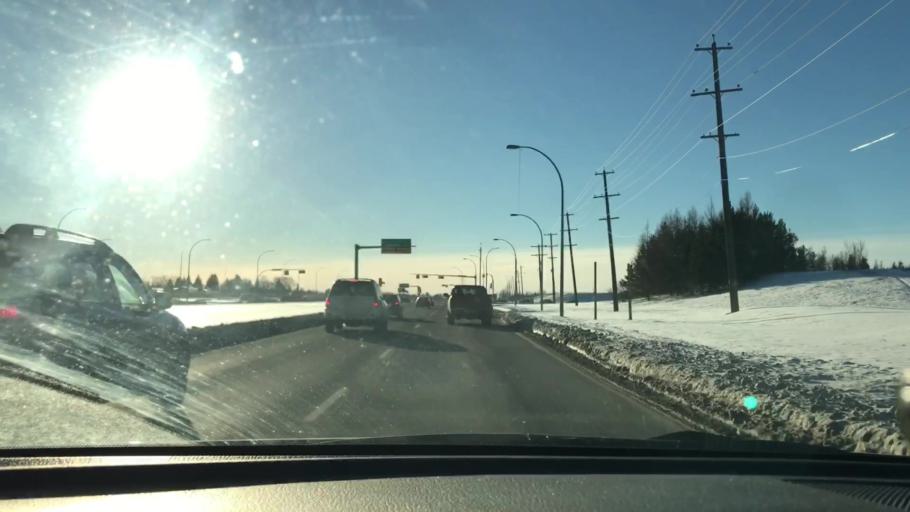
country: CA
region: Alberta
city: Edmonton
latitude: 53.4851
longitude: -113.4673
